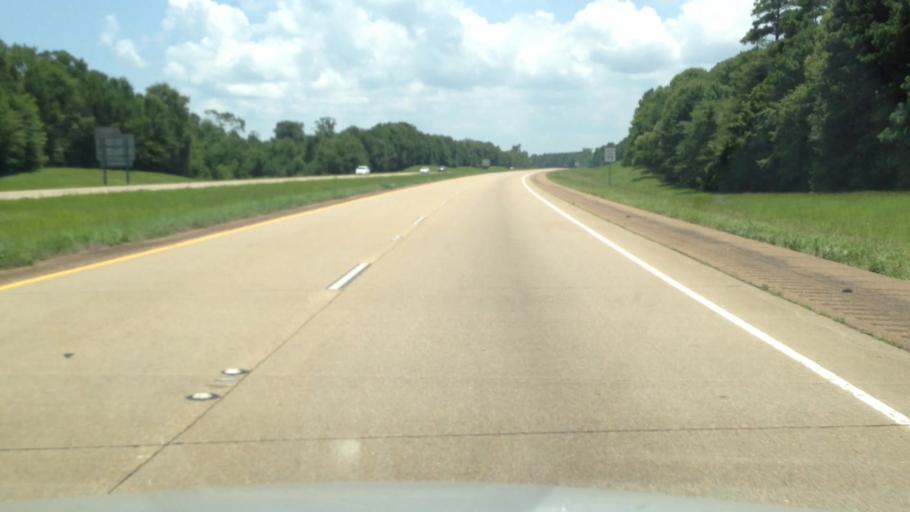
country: US
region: Louisiana
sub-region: Rapides Parish
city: Woodworth
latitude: 31.1534
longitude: -92.4542
